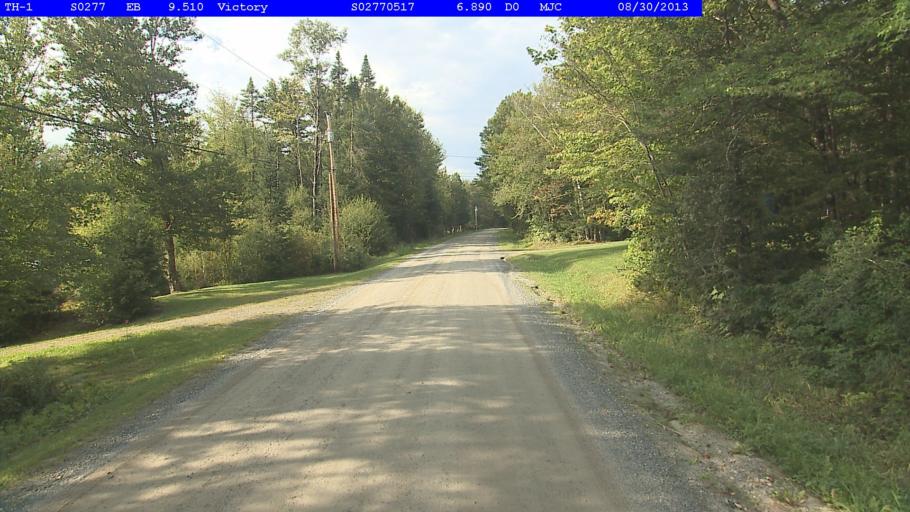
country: US
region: Vermont
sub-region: Caledonia County
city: Lyndonville
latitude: 44.5672
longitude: -71.7893
